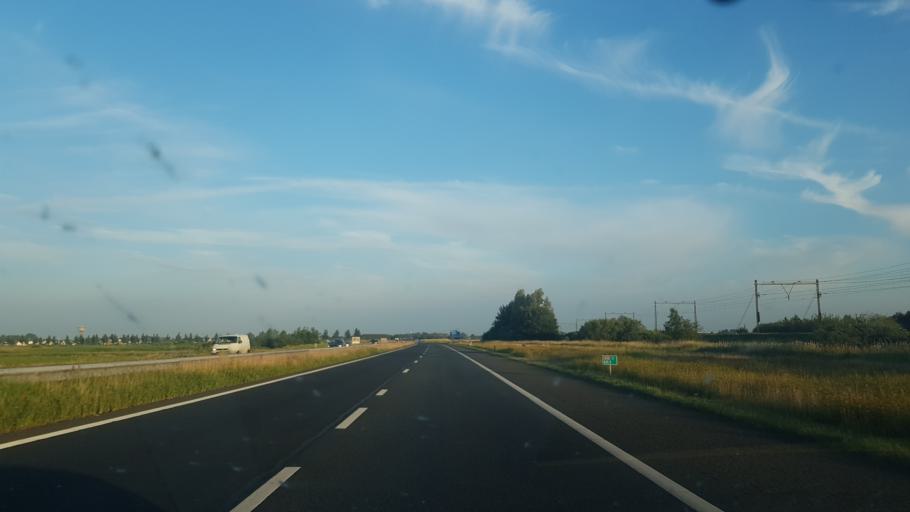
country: NL
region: Friesland
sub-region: Gemeente Boarnsterhim
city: Akkrum
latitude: 53.0659
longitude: 5.8348
